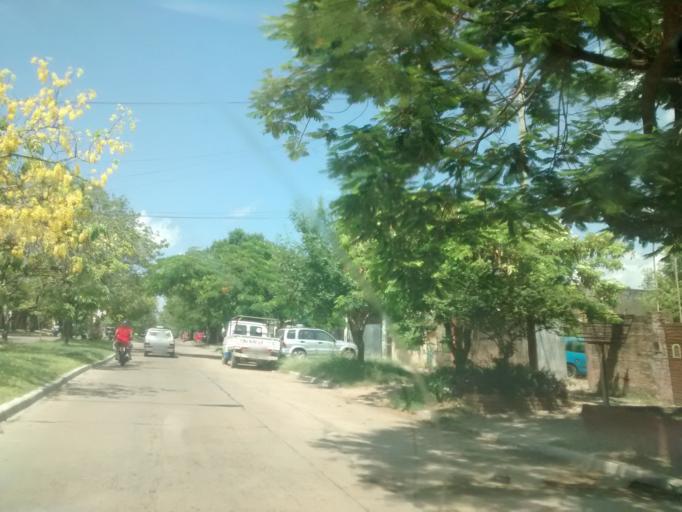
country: AR
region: Chaco
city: Resistencia
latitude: -27.4570
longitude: -58.9719
